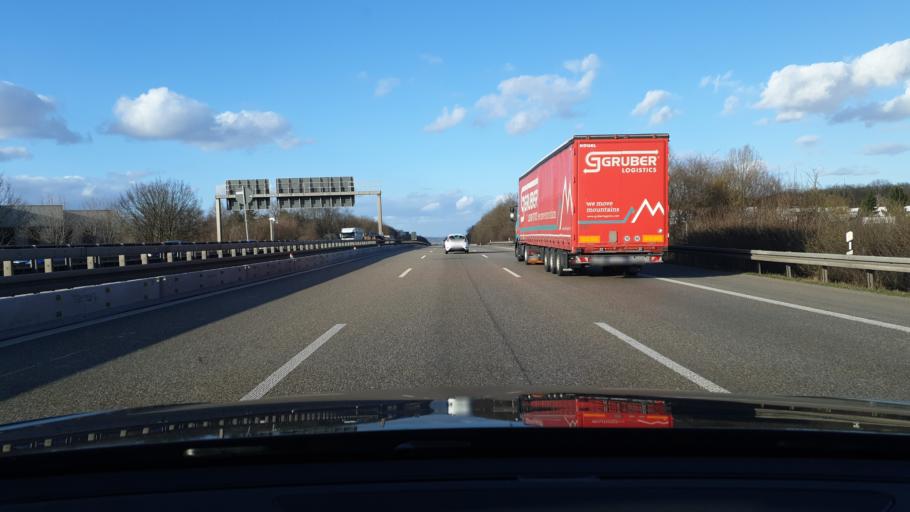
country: DE
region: Baden-Wuerttemberg
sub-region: Regierungsbezirk Stuttgart
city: Asperg
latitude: 48.8907
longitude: 9.1487
